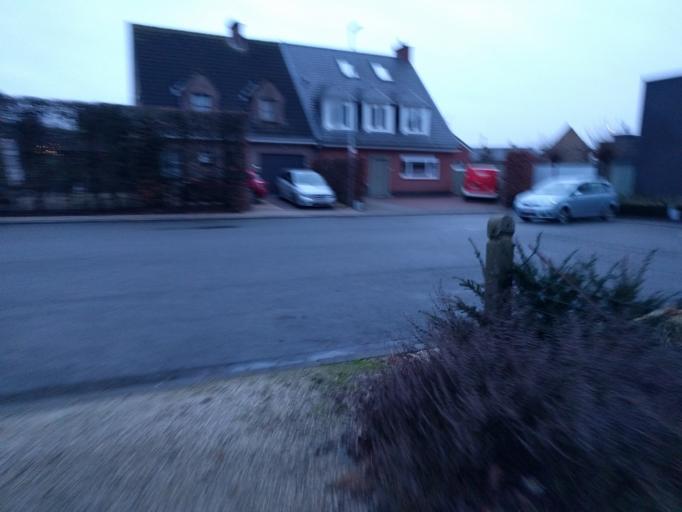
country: BE
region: Flanders
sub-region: Provincie West-Vlaanderen
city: Wevelgem
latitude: 50.8181
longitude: 3.1721
